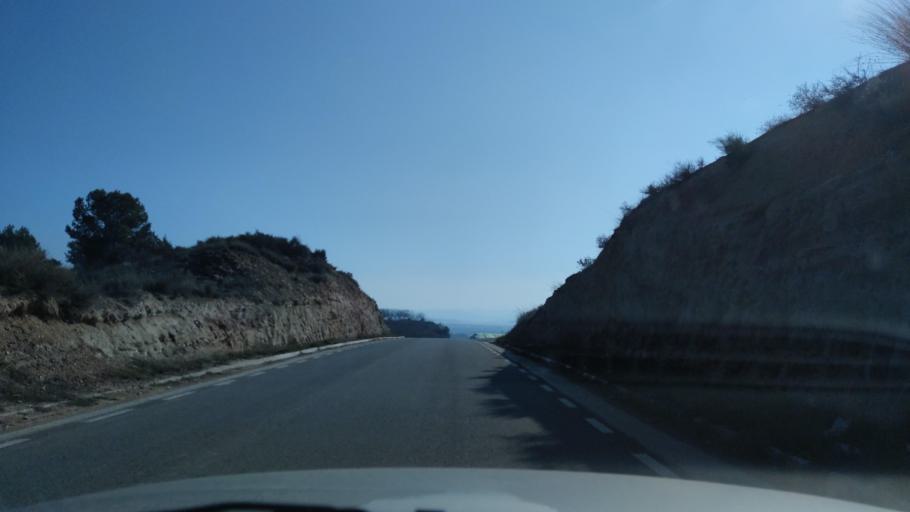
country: ES
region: Catalonia
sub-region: Provincia de Lleida
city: Torrebesses
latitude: 41.4676
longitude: 0.5638
